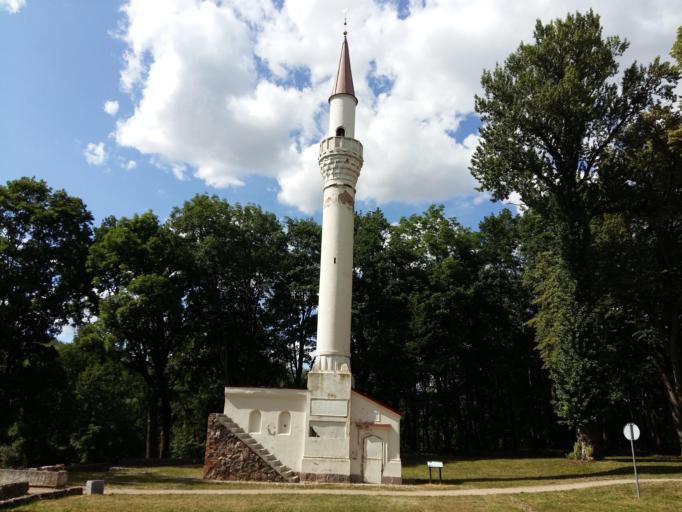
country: LT
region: Kauno apskritis
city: Kedainiai
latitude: 55.3076
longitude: 23.9762
